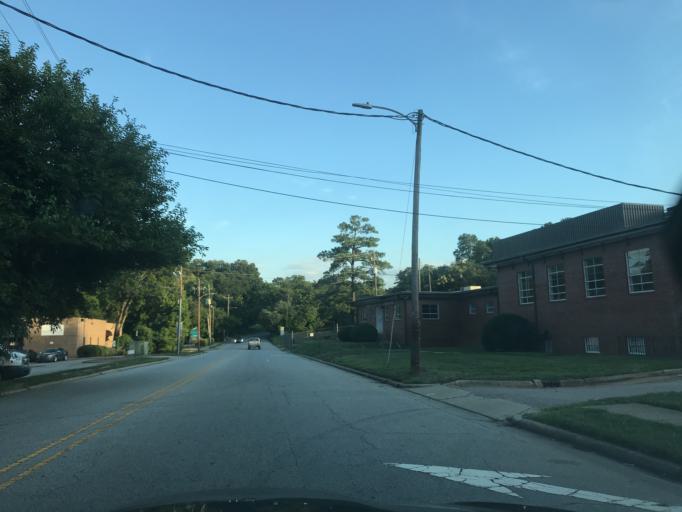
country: US
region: North Carolina
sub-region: Wake County
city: Raleigh
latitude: 35.7993
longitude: -78.6249
